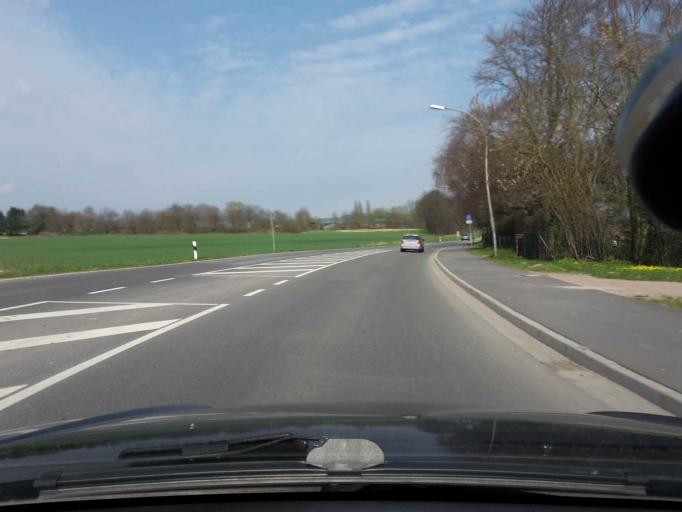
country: DE
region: Lower Saxony
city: Seevetal
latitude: 53.3876
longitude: 9.9740
